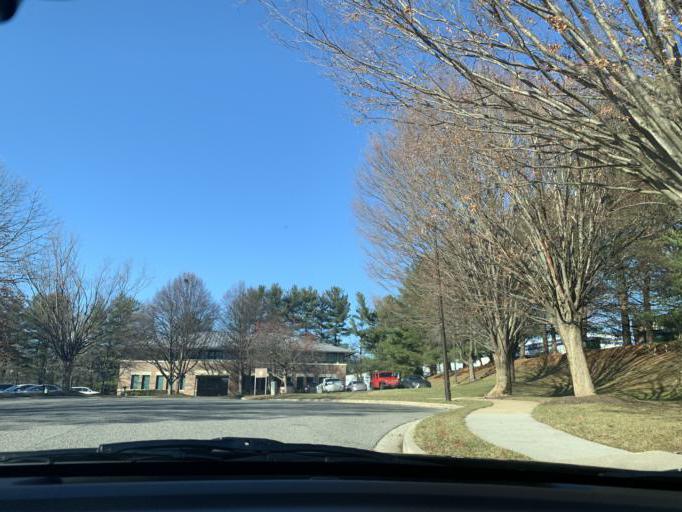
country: US
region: Maryland
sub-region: Baltimore County
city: Garrison
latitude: 39.3998
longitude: -76.7541
